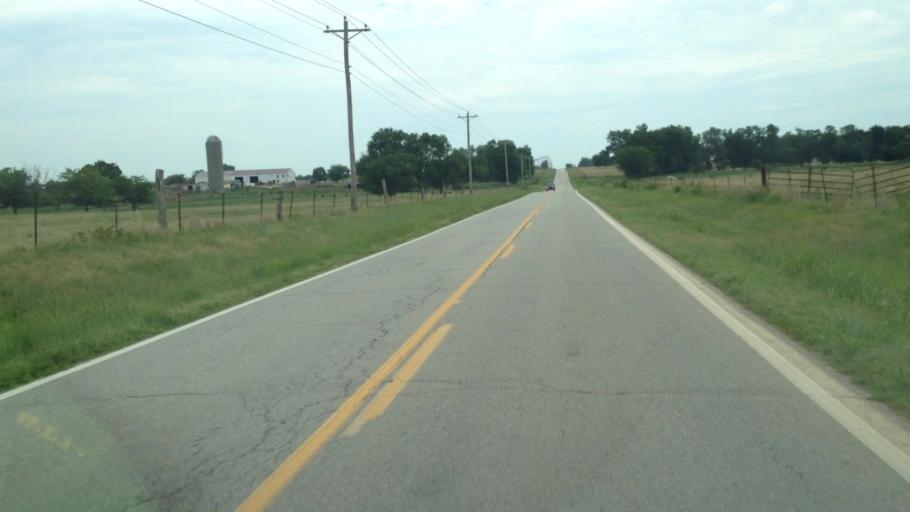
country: US
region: Oklahoma
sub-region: Delaware County
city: Cleora
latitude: 36.6013
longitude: -94.9634
